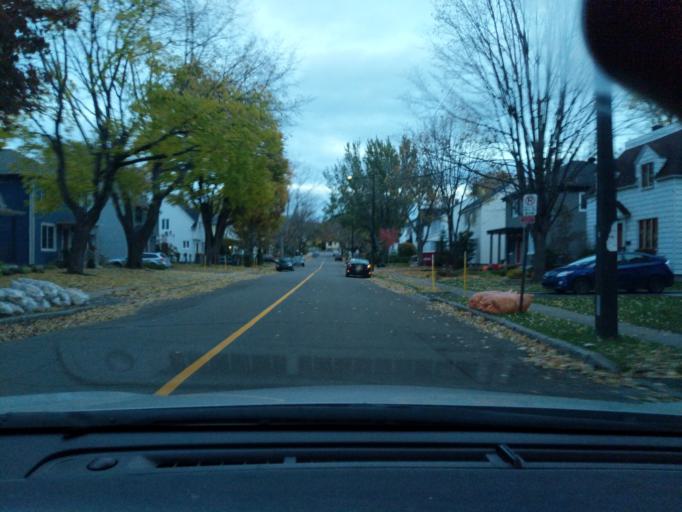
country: CA
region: Quebec
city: Quebec
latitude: 46.7896
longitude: -71.2508
